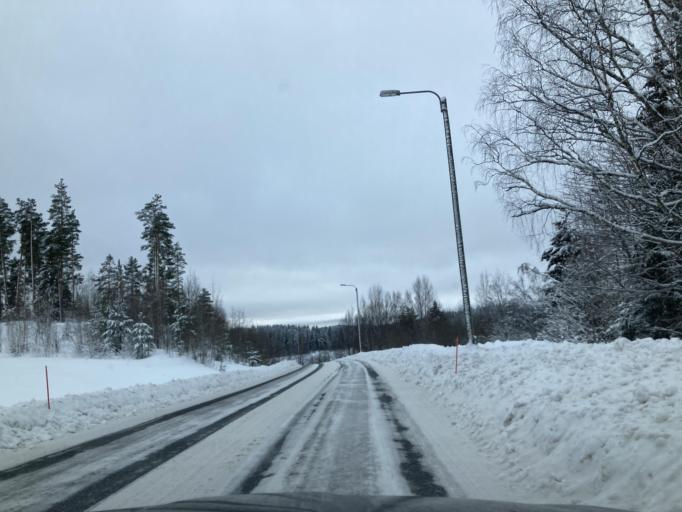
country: FI
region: Central Finland
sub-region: Jaemsae
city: Jaemsae
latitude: 61.8749
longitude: 25.2723
